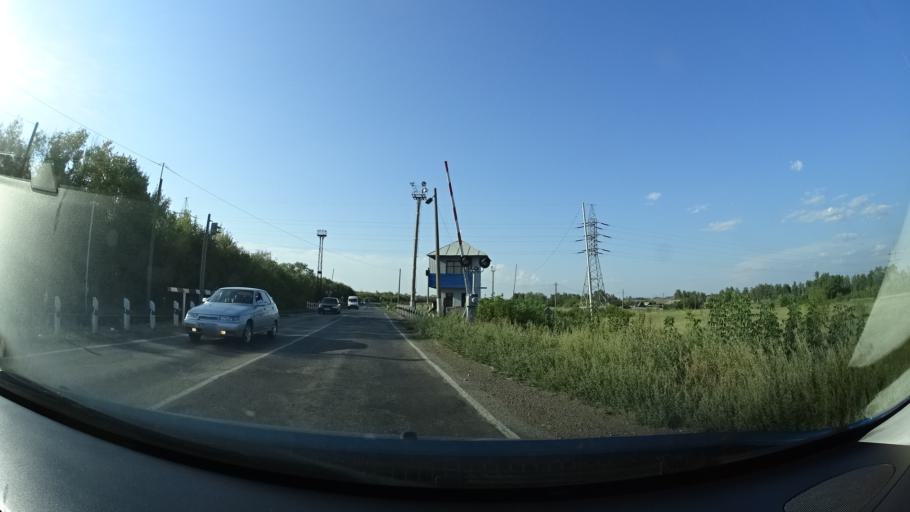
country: RU
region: Bashkortostan
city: Salavat
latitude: 53.4535
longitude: 55.9186
